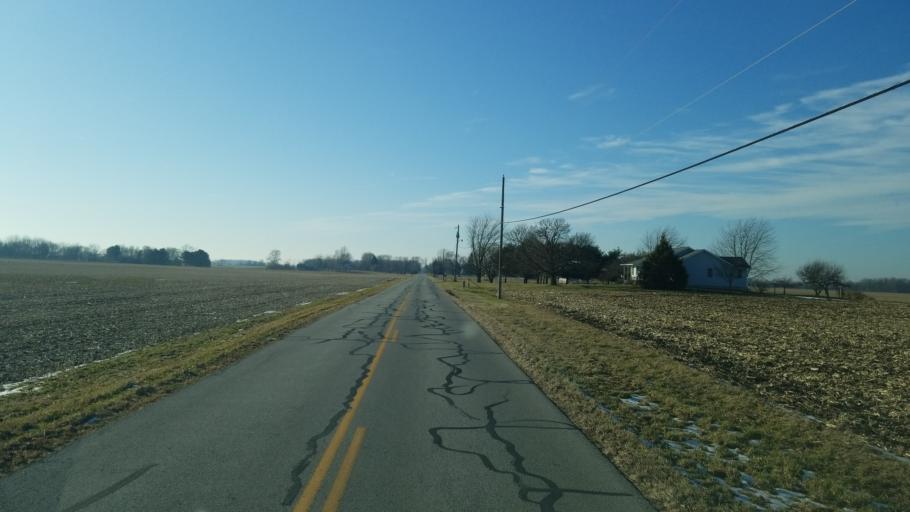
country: US
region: Ohio
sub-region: Sandusky County
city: Mount Carmel
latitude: 41.2705
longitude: -82.9464
